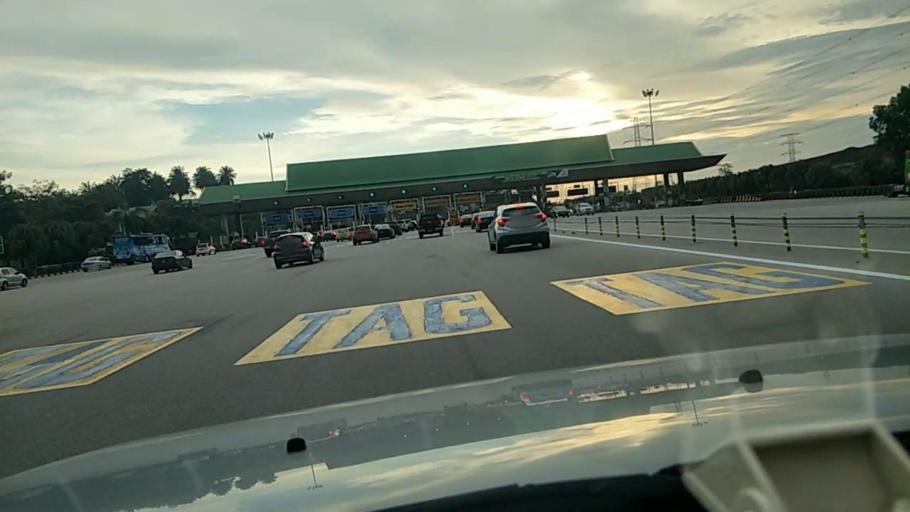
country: MY
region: Selangor
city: Shah Alam
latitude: 3.0918
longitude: 101.4875
